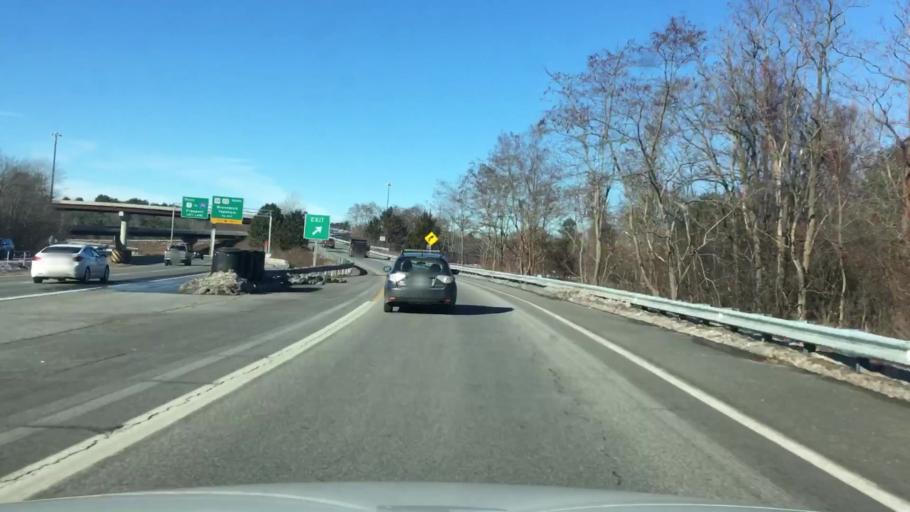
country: US
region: Maine
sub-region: Cumberland County
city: Brunswick
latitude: 43.9188
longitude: -69.9496
